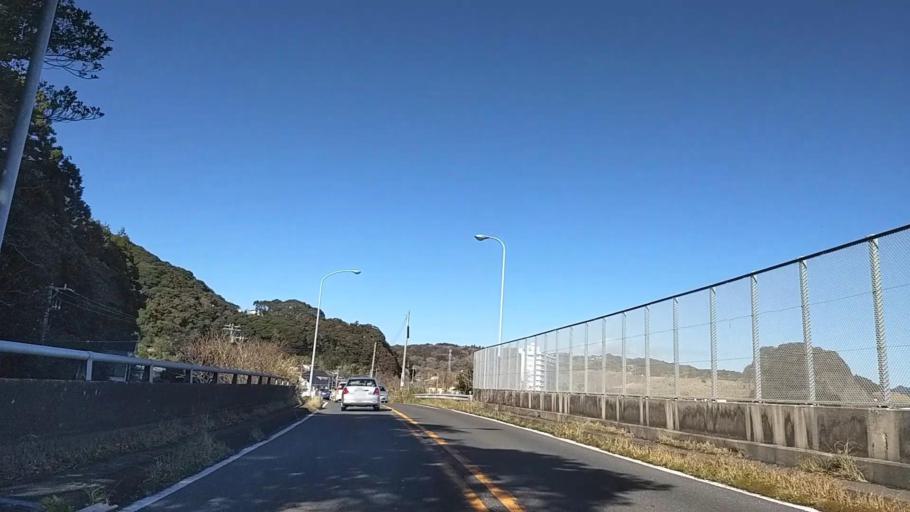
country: JP
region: Chiba
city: Kawaguchi
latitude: 35.0791
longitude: 140.0967
